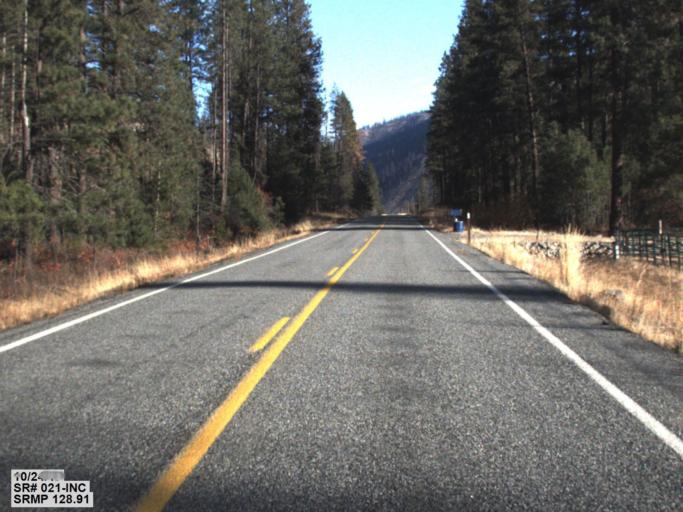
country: US
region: Washington
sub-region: Okanogan County
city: Coulee Dam
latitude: 48.2452
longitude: -118.6936
